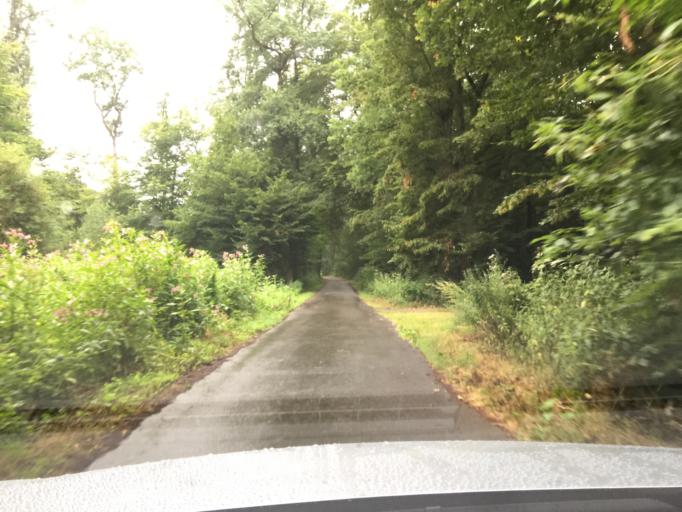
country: DE
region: North Rhine-Westphalia
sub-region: Regierungsbezirk Dusseldorf
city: Ratingen
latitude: 51.3320
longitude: 6.8953
